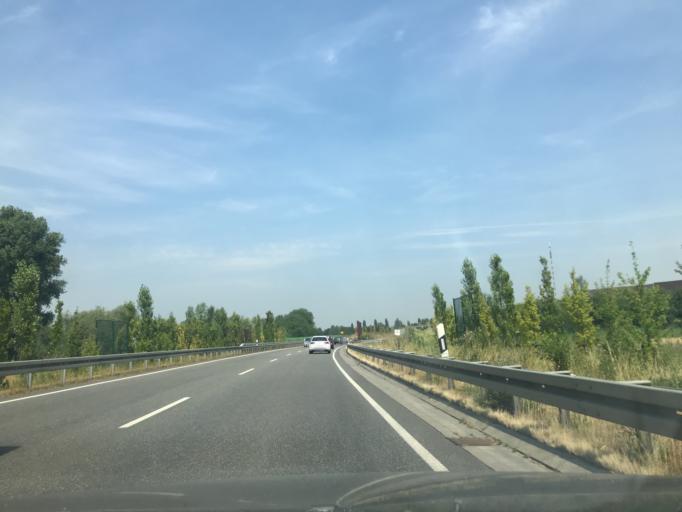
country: DE
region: North Rhine-Westphalia
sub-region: Regierungsbezirk Dusseldorf
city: Alpen
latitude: 51.6305
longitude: 6.5626
